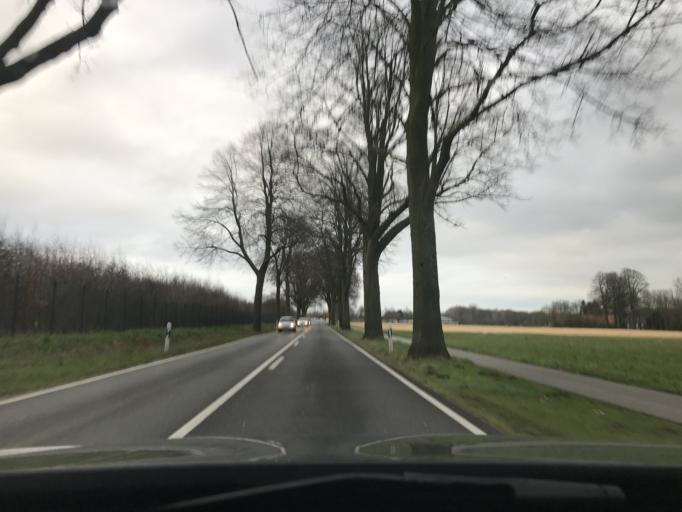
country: DE
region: North Rhine-Westphalia
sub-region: Regierungsbezirk Dusseldorf
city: Uedem
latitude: 51.6466
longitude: 6.2806
